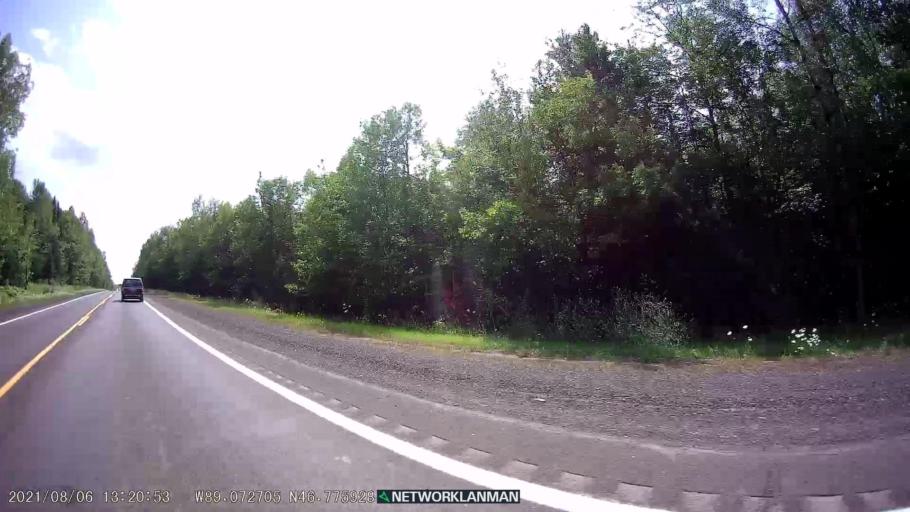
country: US
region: Michigan
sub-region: Ontonagon County
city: Ontonagon
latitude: 46.7758
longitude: -89.0727
